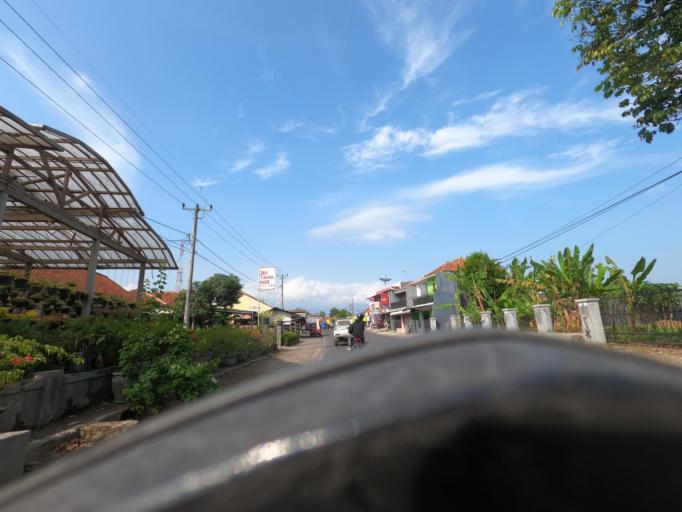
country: ID
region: West Java
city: Lembang
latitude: -6.6547
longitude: 107.7167
